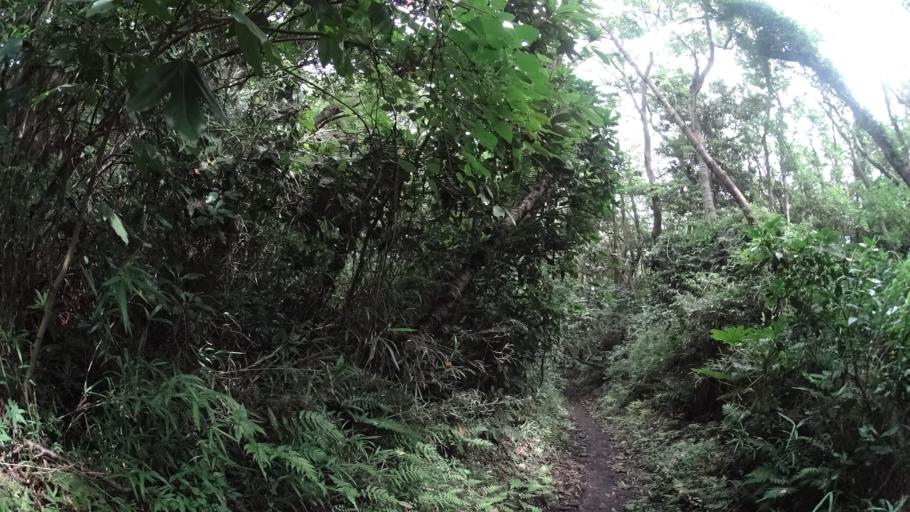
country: JP
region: Kanagawa
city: Yokosuka
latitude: 35.2146
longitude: 139.6563
